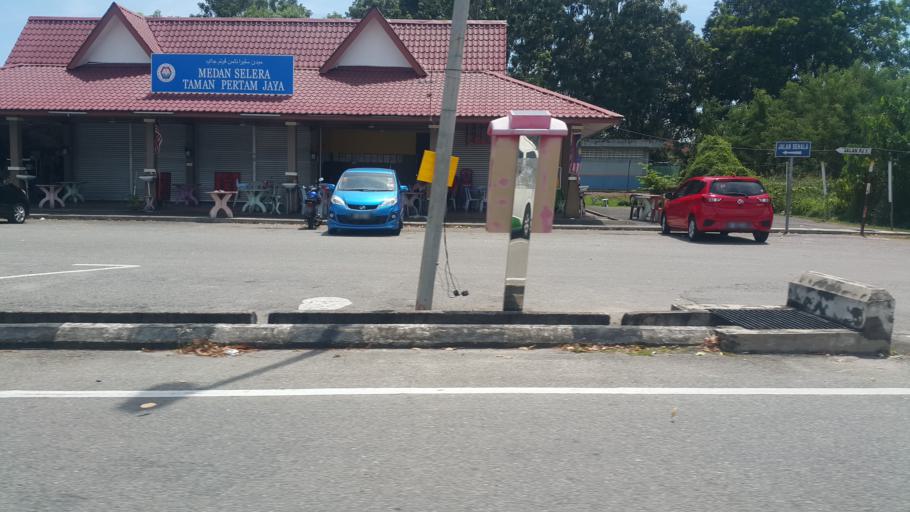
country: MY
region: Melaka
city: Kampung Bukit Baharu
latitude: 2.1889
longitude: 102.2784
